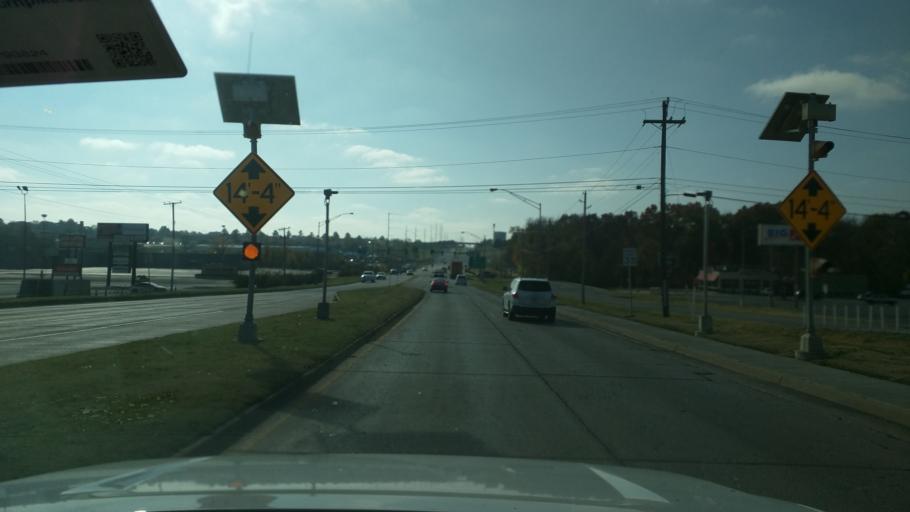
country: US
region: Oklahoma
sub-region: Washington County
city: Bartlesville
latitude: 36.7503
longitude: -95.9356
